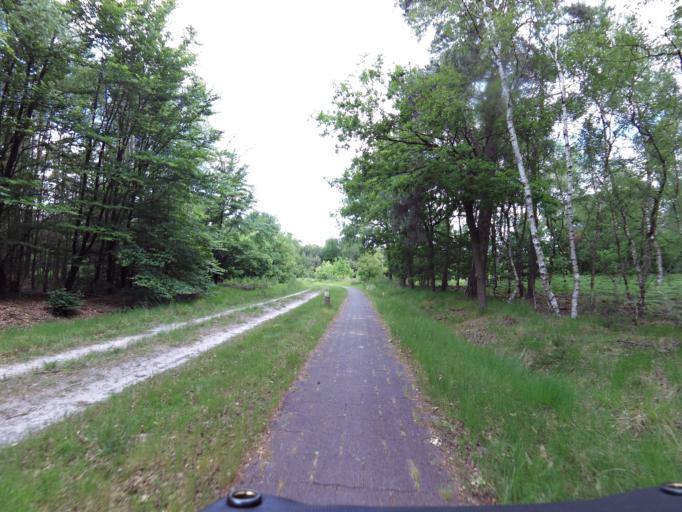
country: NL
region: North Brabant
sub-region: Gemeente Baarle-Nassau
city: Baarle-Nassau
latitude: 51.5038
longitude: 4.9160
